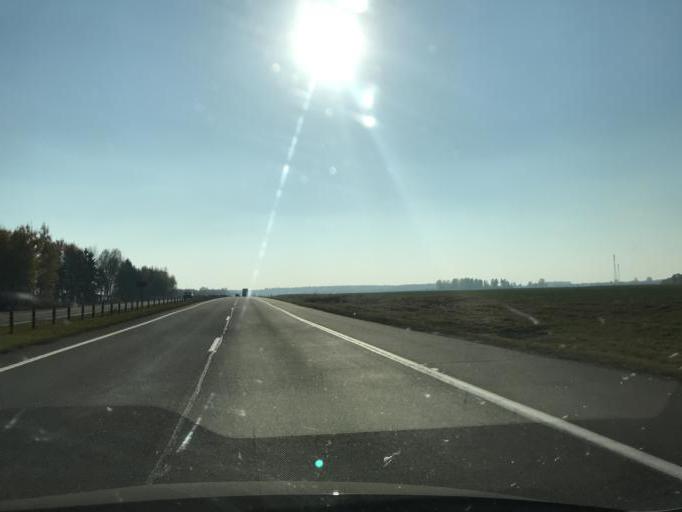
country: BY
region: Minsk
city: Enyerhyetykaw
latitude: 53.6194
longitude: 27.0518
